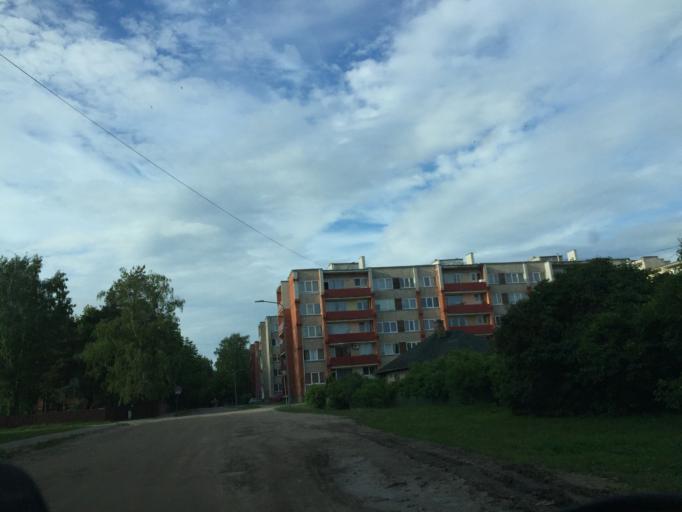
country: LV
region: Valmieras Rajons
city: Valmiera
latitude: 57.5298
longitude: 25.4189
